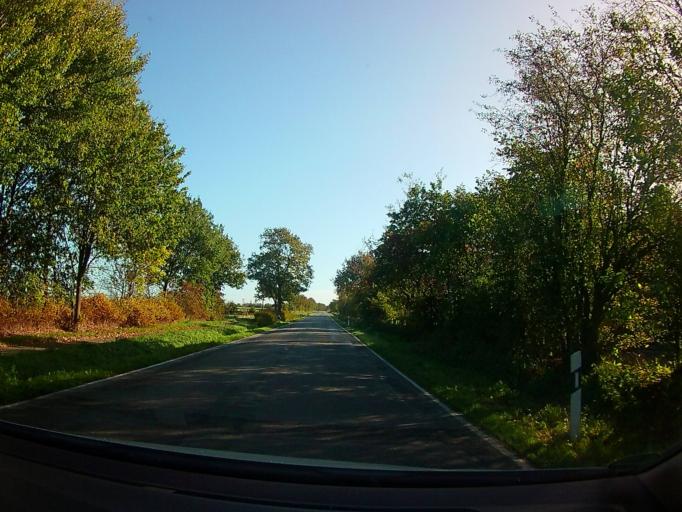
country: DE
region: Schleswig-Holstein
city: Viol
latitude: 54.5669
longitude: 9.1984
